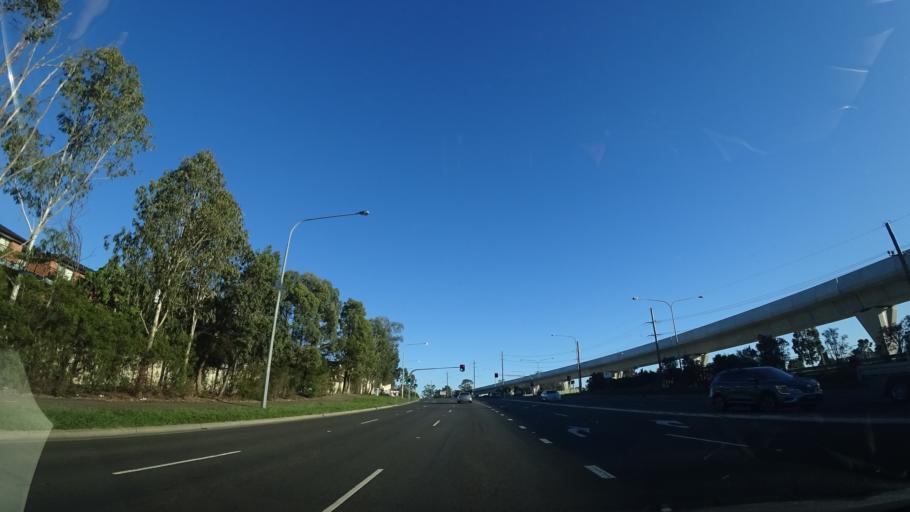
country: AU
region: New South Wales
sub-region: The Hills Shire
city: Beaumont Hills
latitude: -33.6978
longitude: 150.9279
